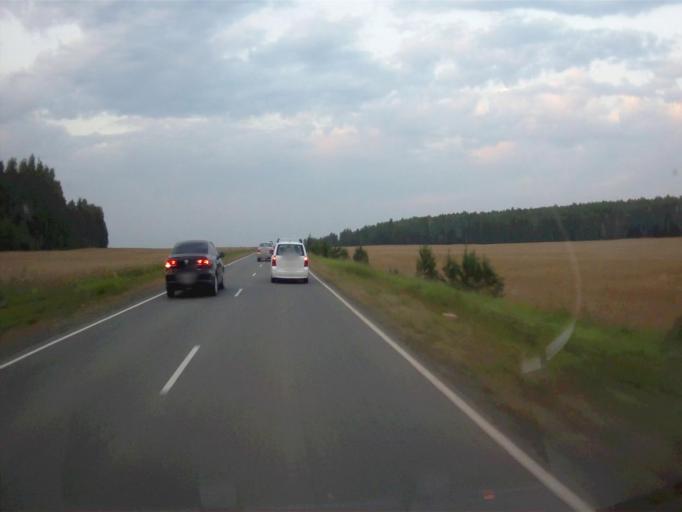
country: RU
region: Chelyabinsk
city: Chebarkul'
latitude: 55.1684
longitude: 60.4490
